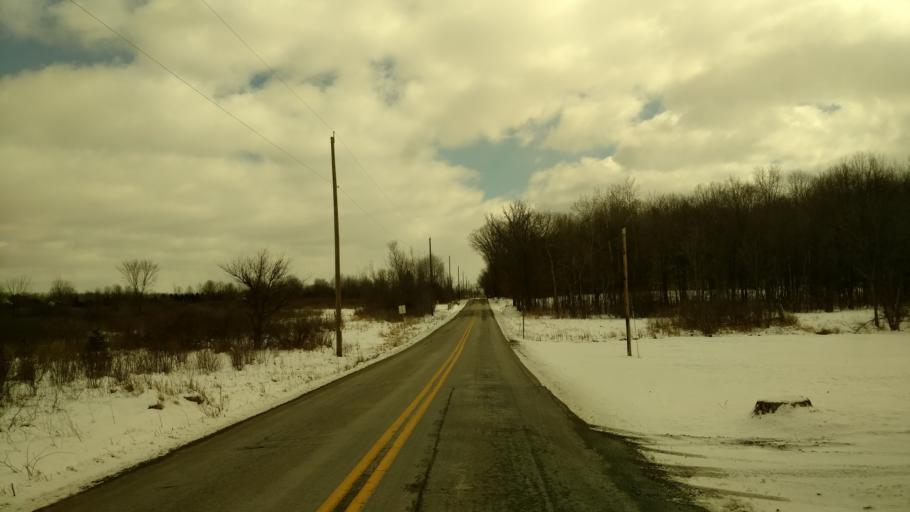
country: US
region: Pennsylvania
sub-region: Mercer County
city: Mercer
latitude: 41.3496
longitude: -80.2311
